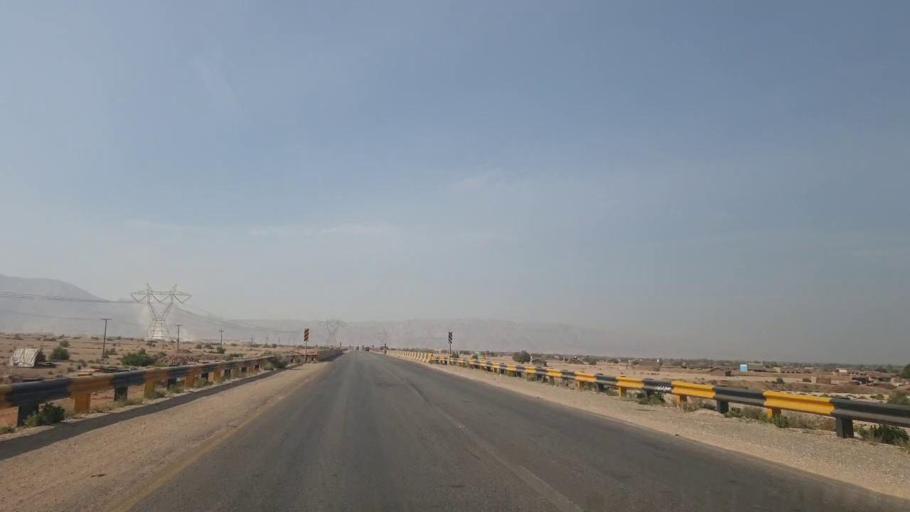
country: PK
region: Sindh
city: Sehwan
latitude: 26.2054
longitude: 67.9312
